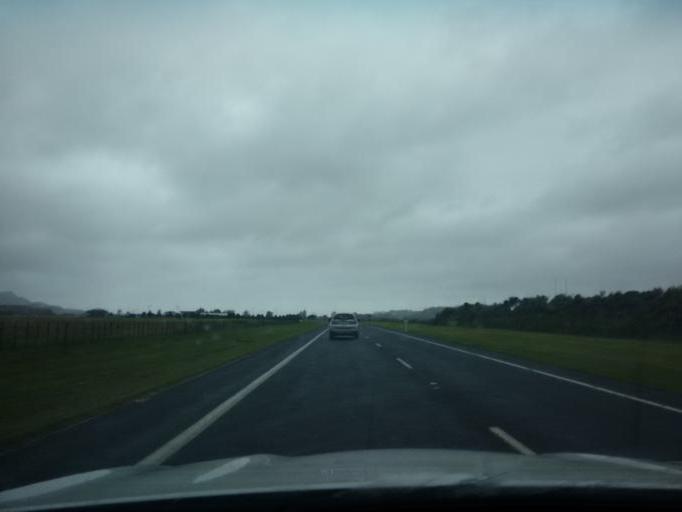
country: NZ
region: Waikato
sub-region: Thames-Coromandel District
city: Whitianga
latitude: -36.8326
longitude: 175.6784
